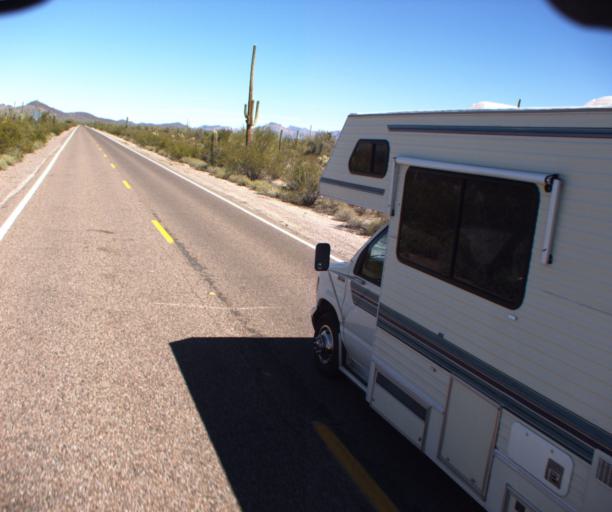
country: MX
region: Sonora
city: Sonoyta
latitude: 31.8967
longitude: -112.8118
